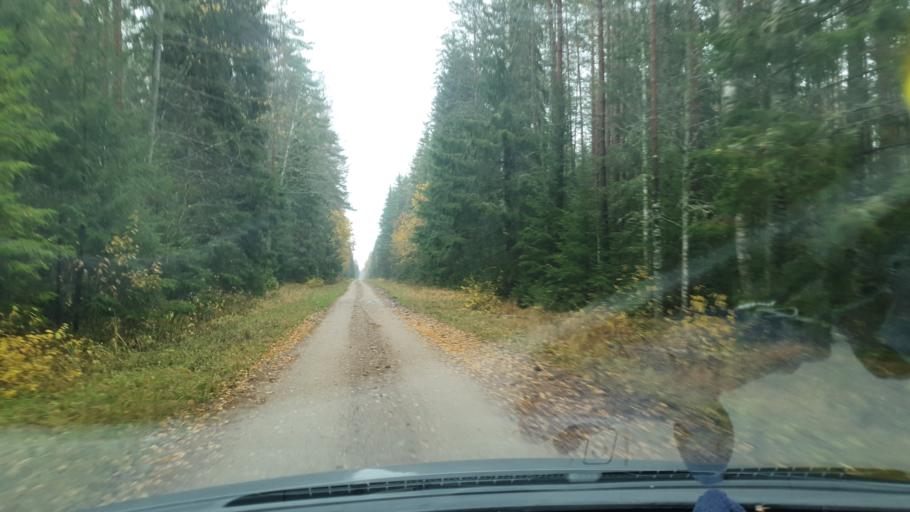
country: EE
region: Viljandimaa
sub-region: Karksi vald
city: Karksi-Nuia
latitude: 57.9772
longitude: 25.6227
